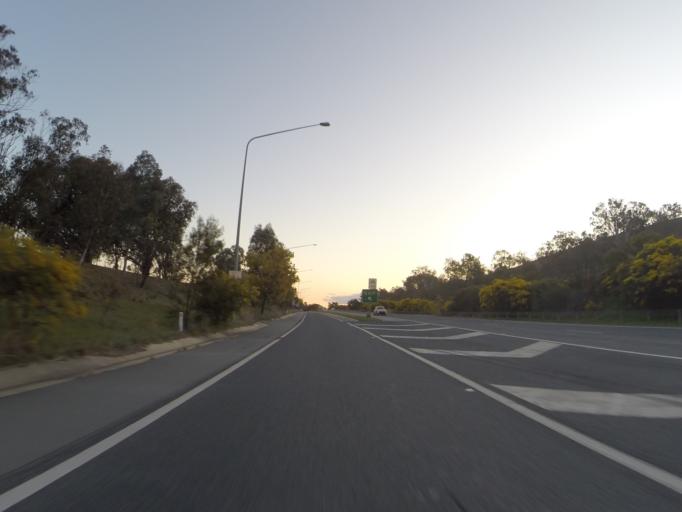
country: AU
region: Australian Capital Territory
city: Kaleen
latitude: -35.2084
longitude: 149.1927
